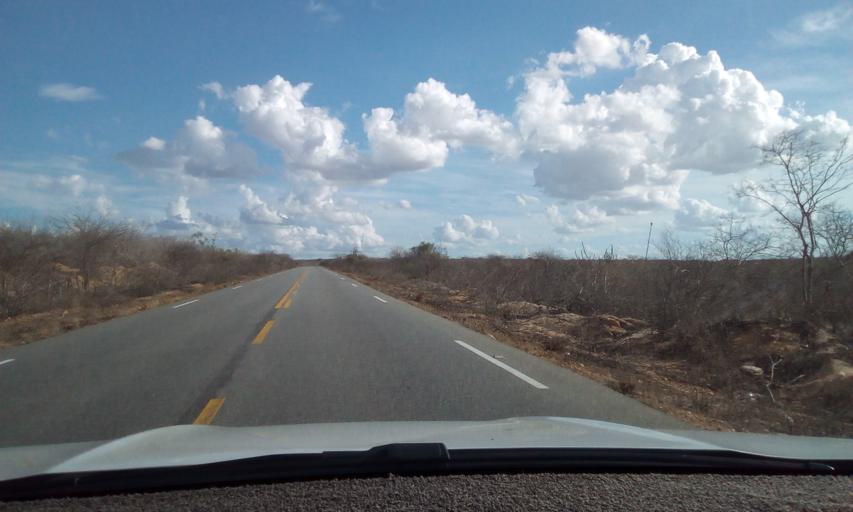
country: BR
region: Paraiba
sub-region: Soledade
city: Soledade
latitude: -6.8704
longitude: -36.4011
